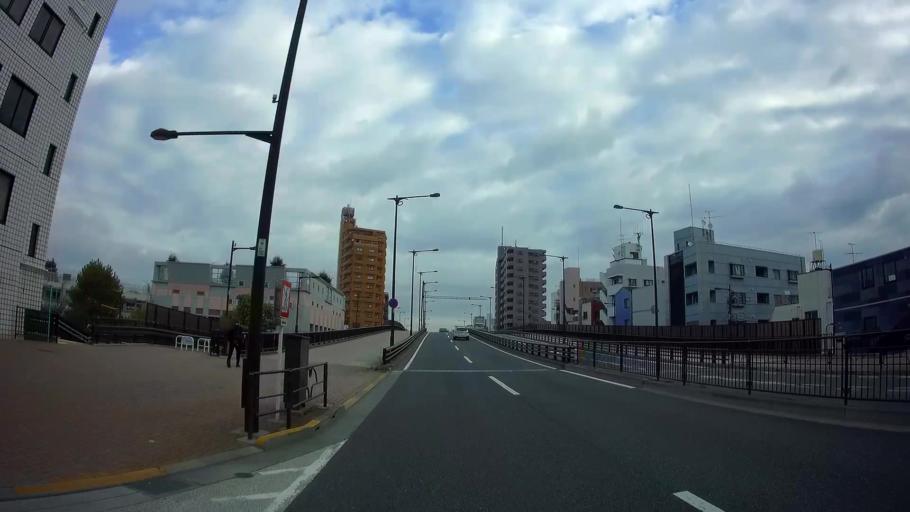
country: JP
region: Tokyo
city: Tokyo
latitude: 35.7139
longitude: 139.6863
